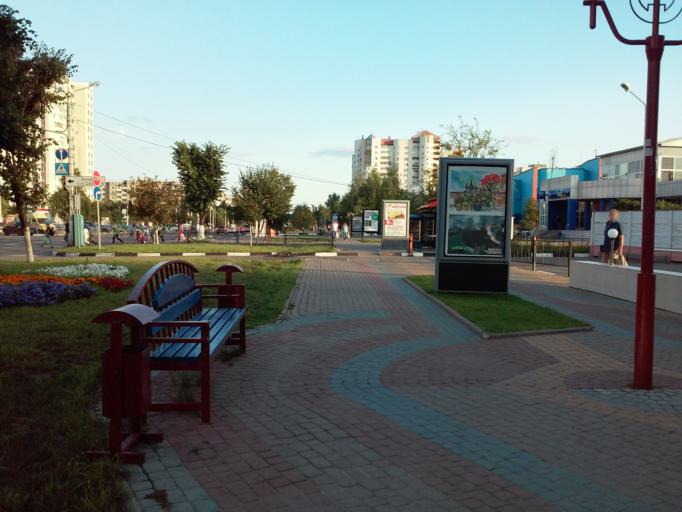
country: RU
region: Belgorod
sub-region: Belgorodskiy Rayon
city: Belgorod
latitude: 50.5759
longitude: 36.5826
